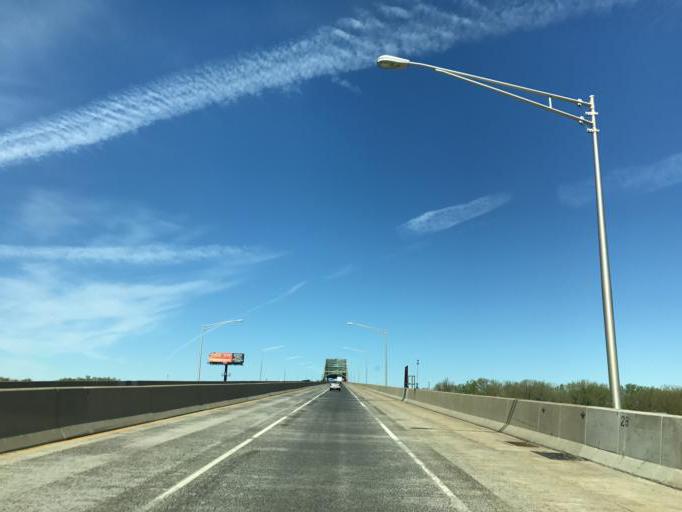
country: US
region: Pennsylvania
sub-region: Bucks County
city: Tullytown
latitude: 40.1147
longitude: -74.8219
